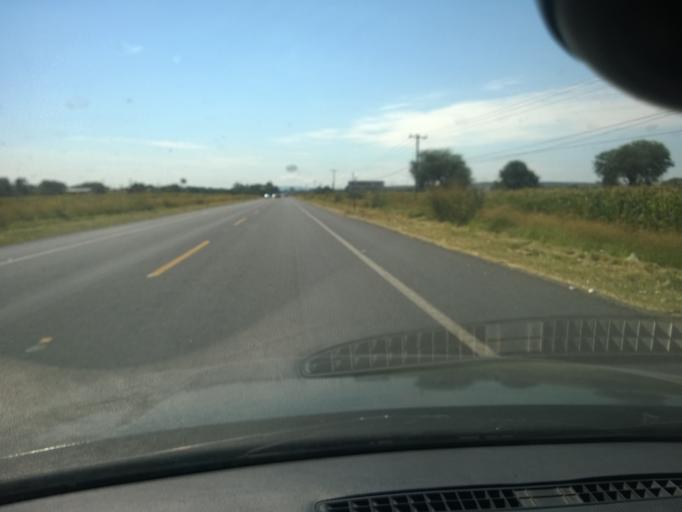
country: MX
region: Guanajuato
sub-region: Leon
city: El CERESO
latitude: 21.0148
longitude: -101.6996
